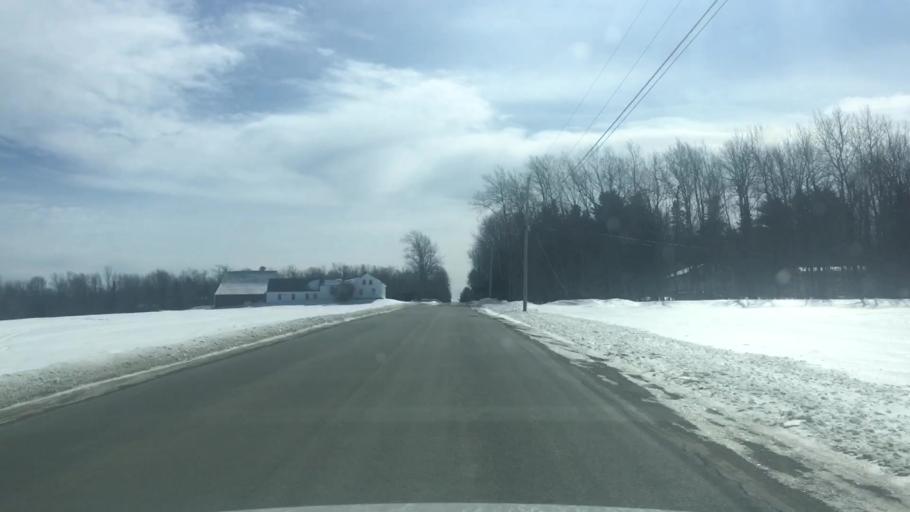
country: US
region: Maine
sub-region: Penobscot County
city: Holden
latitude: 44.7757
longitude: -68.6509
